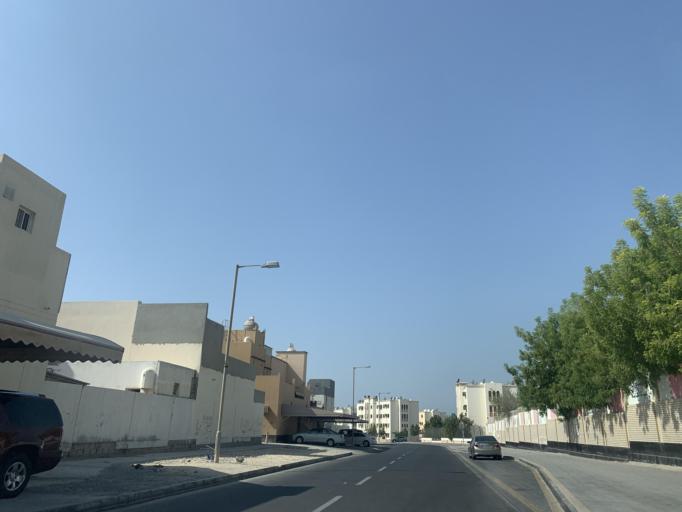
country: BH
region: Central Governorate
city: Madinat Hamad
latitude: 26.1320
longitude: 50.5028
